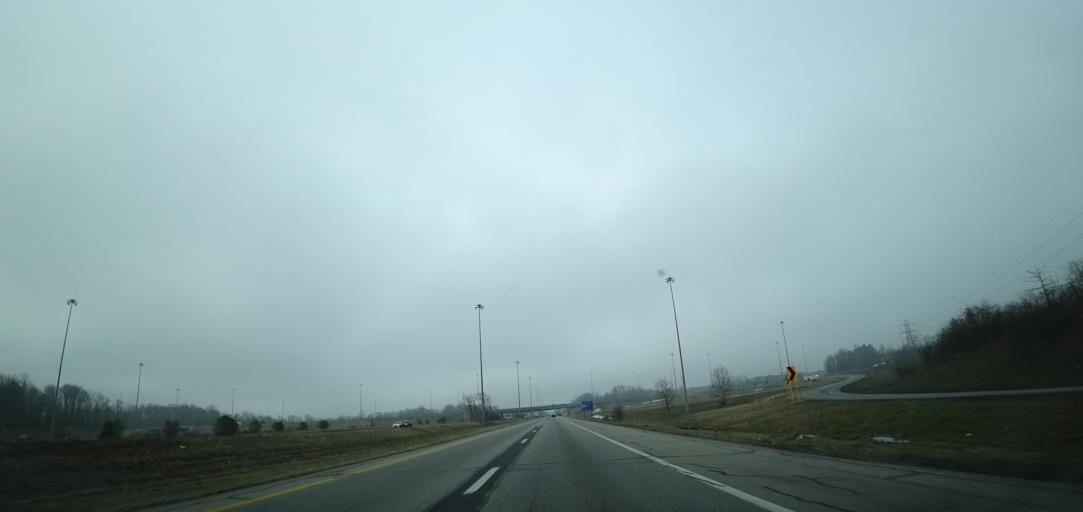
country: US
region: Ohio
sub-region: Summit County
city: Richfield
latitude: 41.2325
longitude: -81.6280
